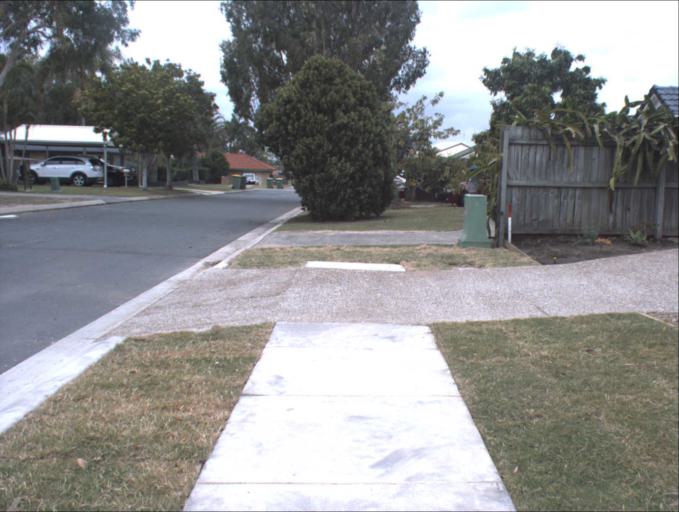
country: AU
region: Queensland
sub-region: Logan
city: Park Ridge South
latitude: -27.6786
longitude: 153.0471
